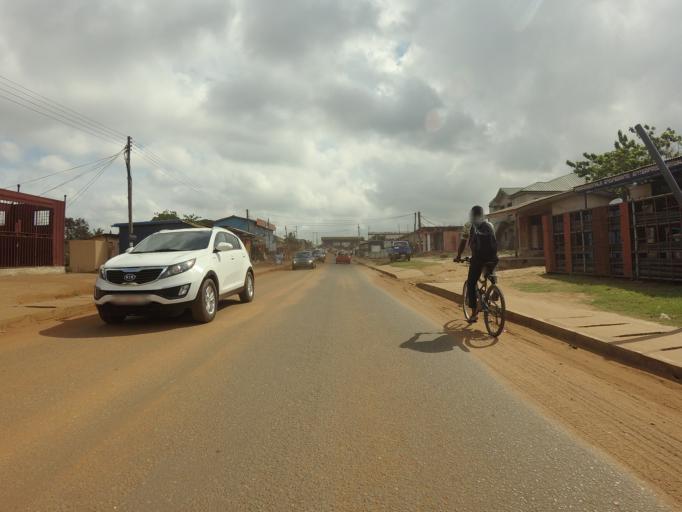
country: GH
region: Greater Accra
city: Teshi Old Town
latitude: 5.5965
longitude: -0.1194
